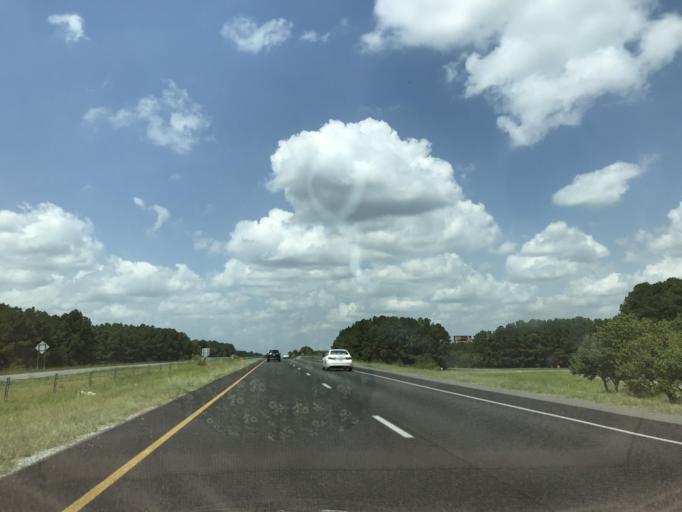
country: US
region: North Carolina
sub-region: Duplin County
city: Wallace
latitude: 34.7679
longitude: -77.9632
